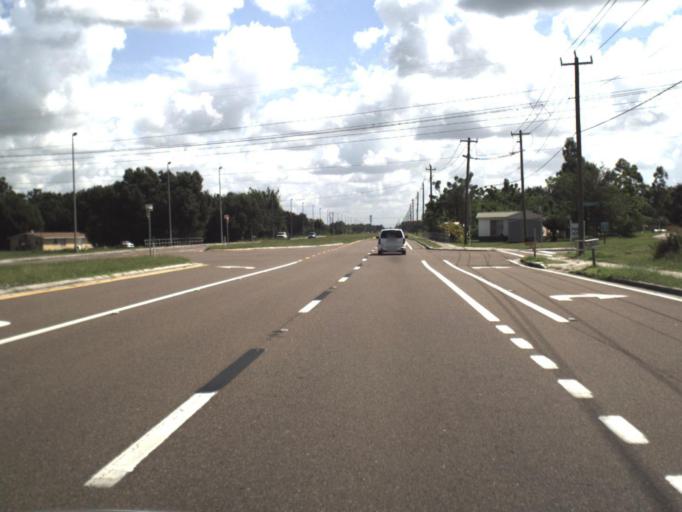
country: US
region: Florida
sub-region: Charlotte County
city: Cleveland
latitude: 26.9639
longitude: -81.9786
